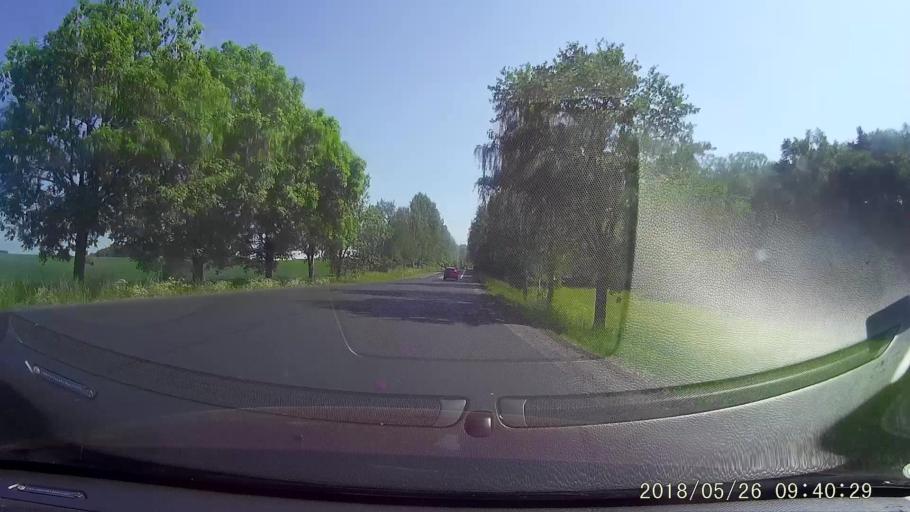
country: PL
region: Lower Silesian Voivodeship
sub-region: Powiat lubanski
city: Siekierczyn
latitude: 51.1605
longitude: 15.1366
